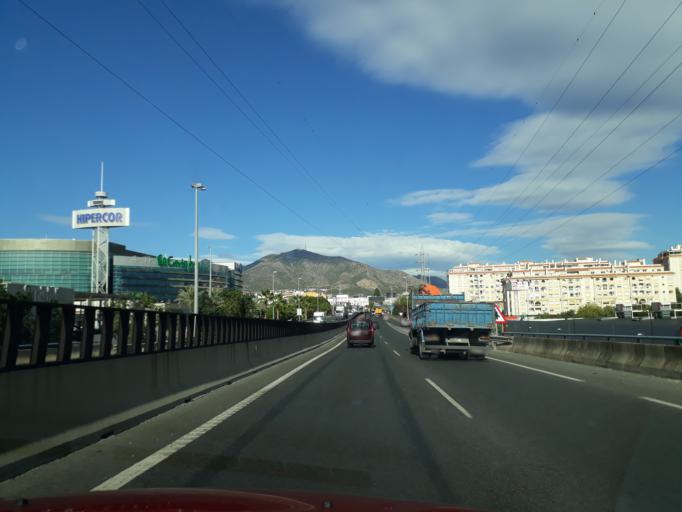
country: ES
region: Andalusia
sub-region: Provincia de Malaga
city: Fuengirola
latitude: 36.5463
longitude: -4.6324
